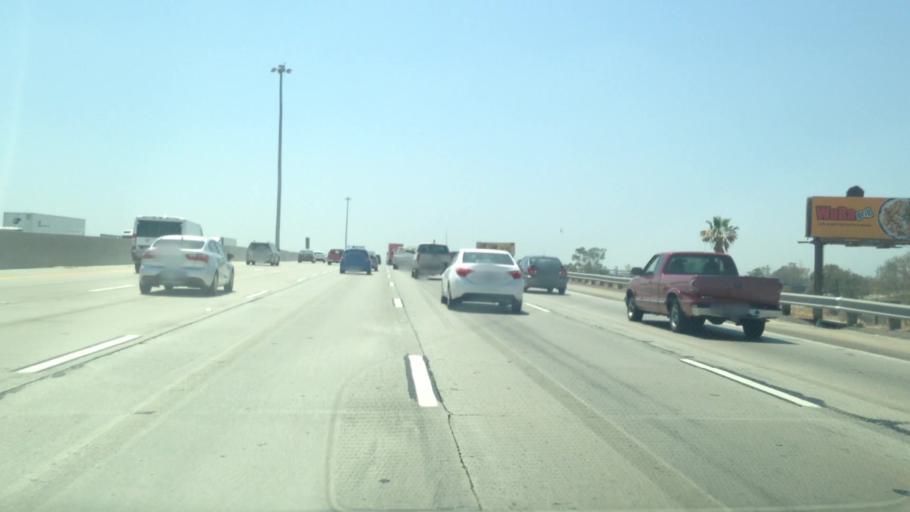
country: US
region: California
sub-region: Riverside County
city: Mira Loma
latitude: 34.0183
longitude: -117.5250
